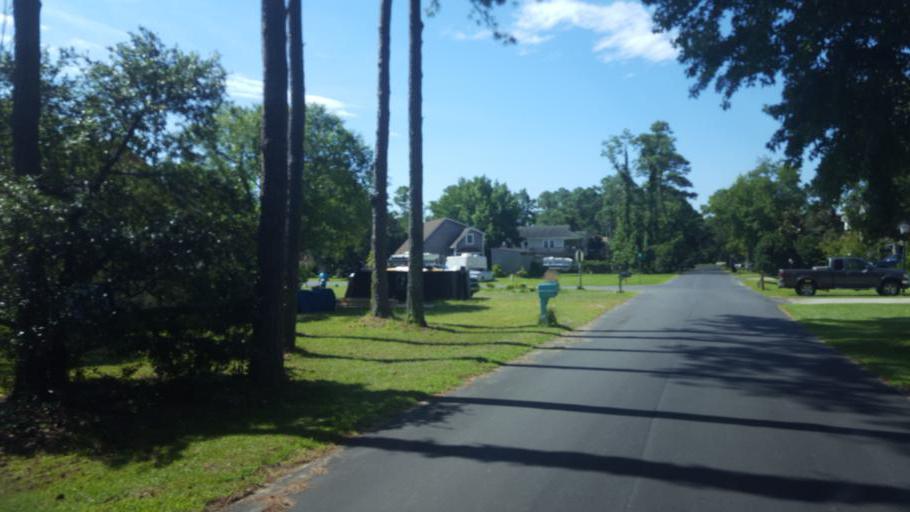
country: US
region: North Carolina
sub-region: Dare County
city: Kill Devil Hills
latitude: 36.0090
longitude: -75.6776
